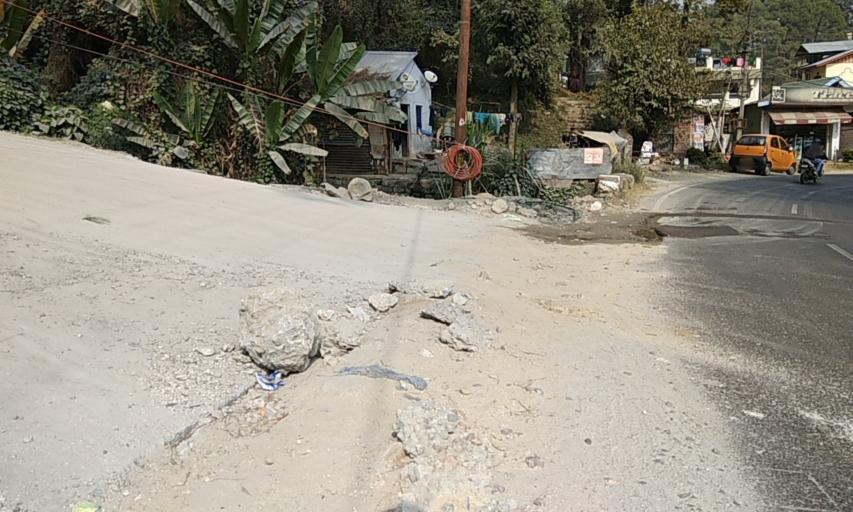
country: IN
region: Himachal Pradesh
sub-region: Kangra
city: Palampur
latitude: 32.1118
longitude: 76.5383
